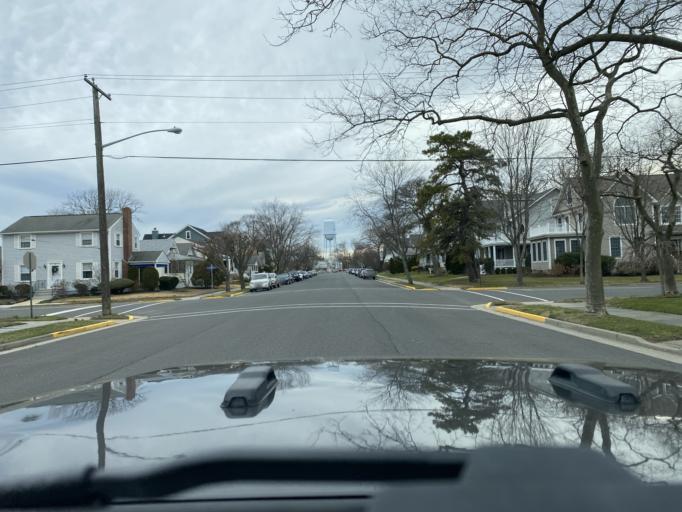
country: US
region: New Jersey
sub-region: Monmouth County
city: Avon-by-the-Sea
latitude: 40.1935
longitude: -74.0177
